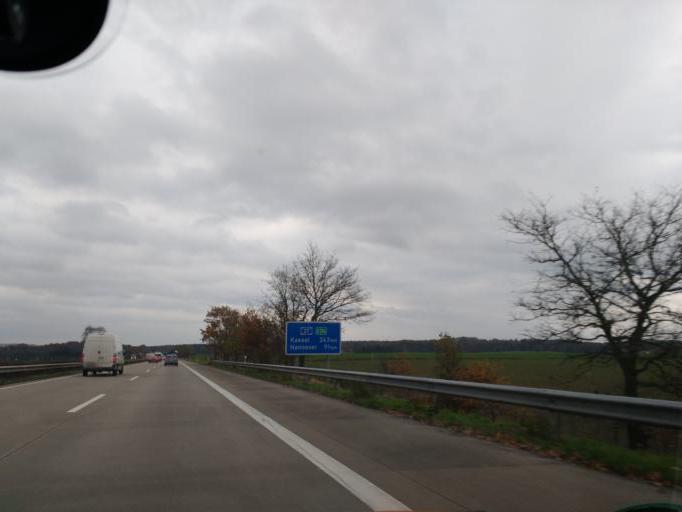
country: DE
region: Lower Saxony
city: Verden
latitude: 52.9543
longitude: 9.2500
